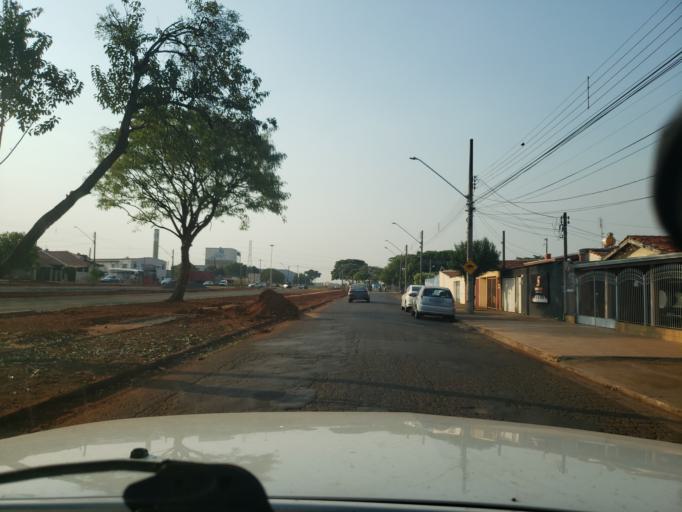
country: BR
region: Sao Paulo
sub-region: Moji-Guacu
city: Mogi-Gaucu
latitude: -22.3426
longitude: -46.9413
